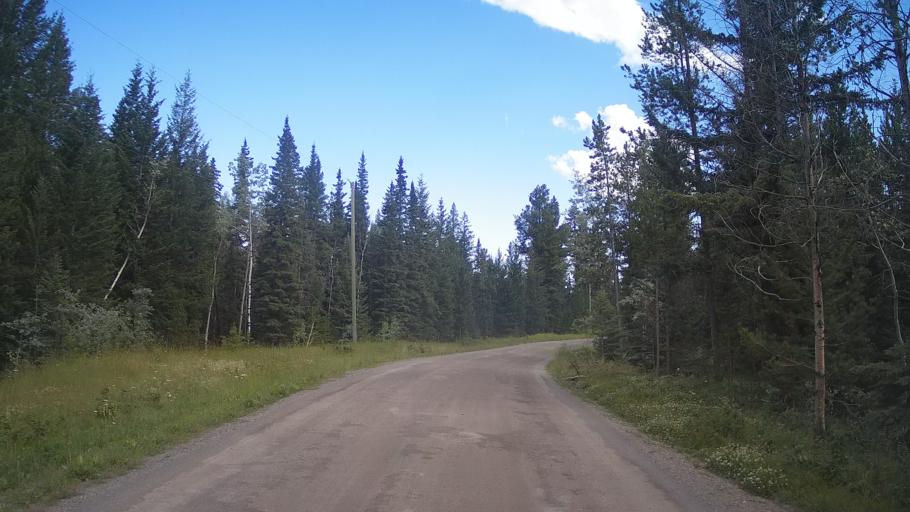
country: CA
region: British Columbia
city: Cache Creek
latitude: 51.1947
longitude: -121.5897
